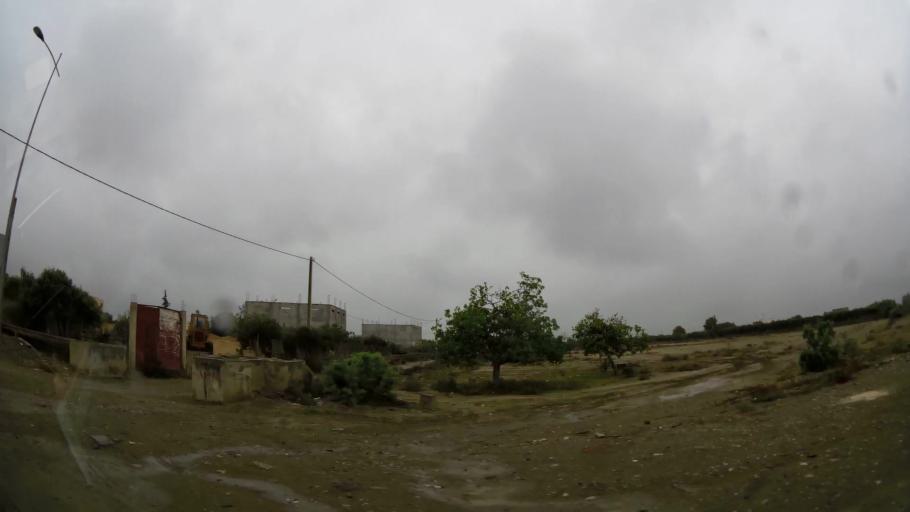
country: MA
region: Taza-Al Hoceima-Taounate
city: Imzourene
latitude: 35.1545
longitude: -3.8315
